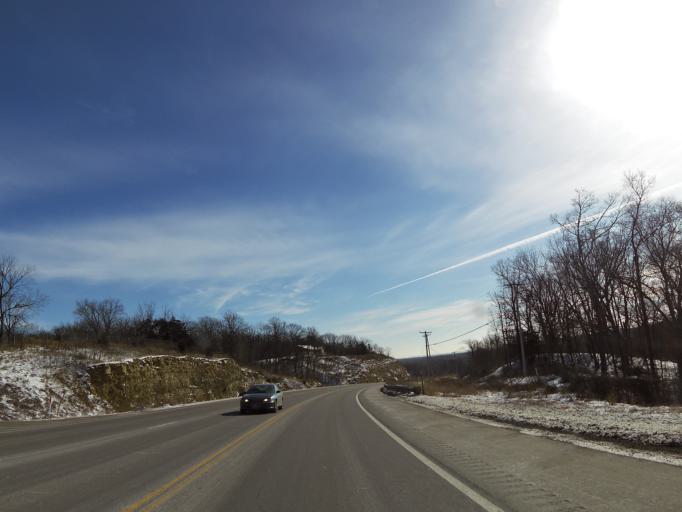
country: US
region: Wisconsin
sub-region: Pierce County
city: Prescott
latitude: 44.7547
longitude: -92.8267
